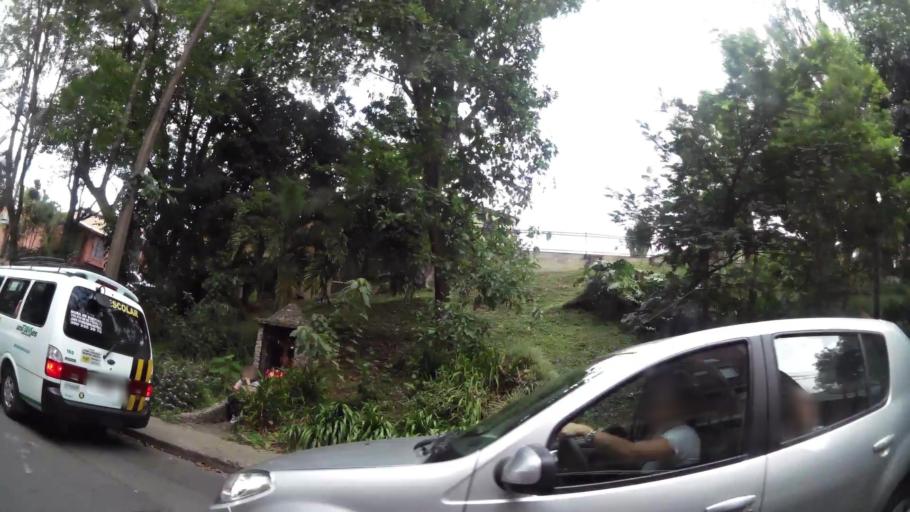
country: CO
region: Antioquia
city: Envigado
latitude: 6.1611
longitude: -75.5936
